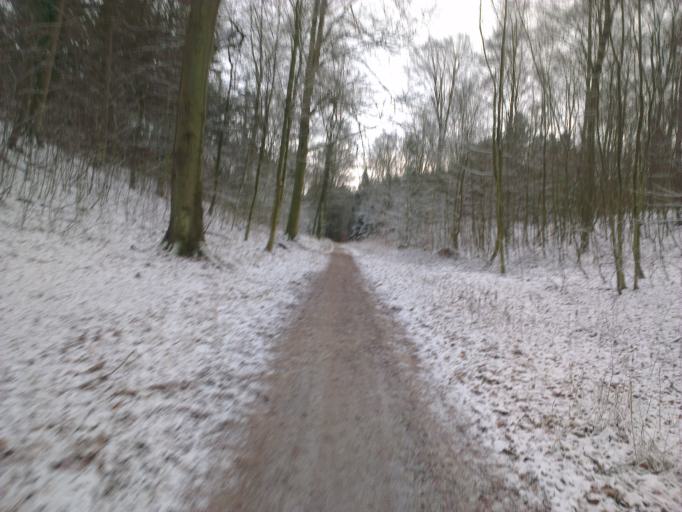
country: DK
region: Capital Region
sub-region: Frederikssund Kommune
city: Frederikssund
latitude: 55.8482
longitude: 12.0213
